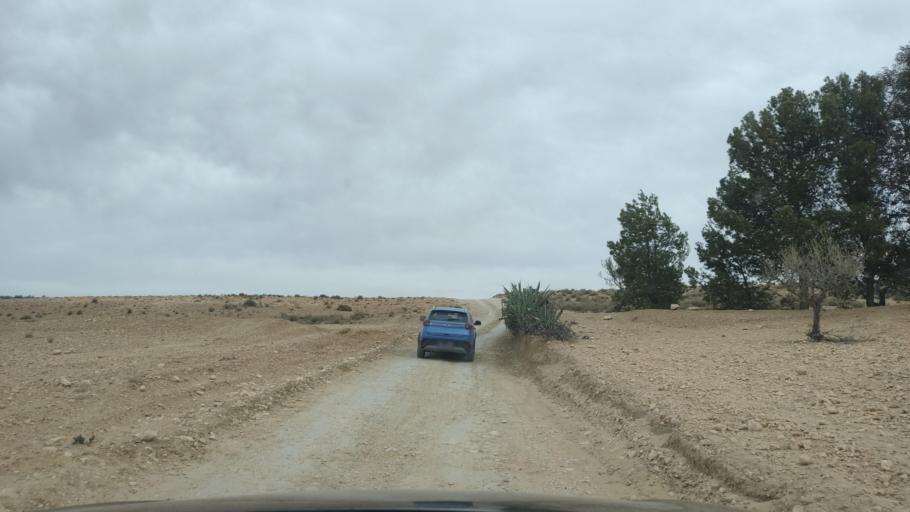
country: TN
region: Al Qasrayn
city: Kasserine
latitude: 35.2571
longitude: 8.9232
